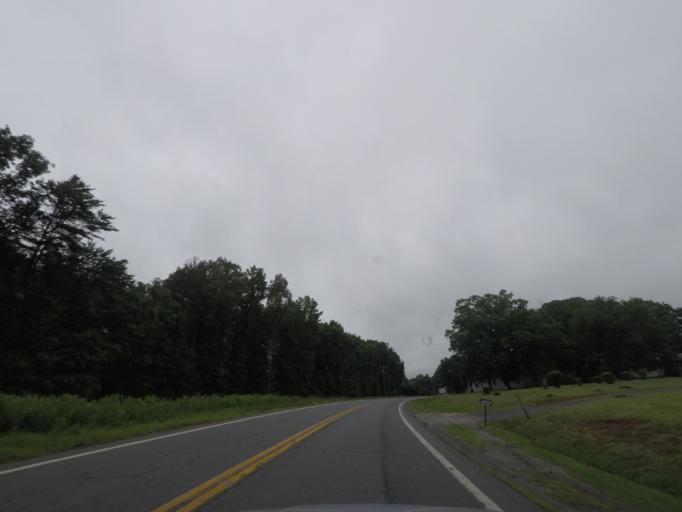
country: US
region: Virginia
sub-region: Fluvanna County
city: Weber City
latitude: 37.6582
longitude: -78.3500
